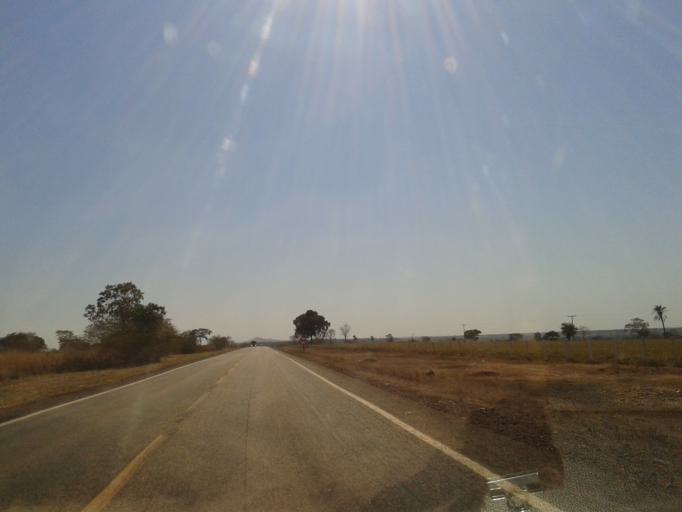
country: BR
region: Goias
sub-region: Crixas
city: Crixas
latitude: -14.1976
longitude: -50.3864
